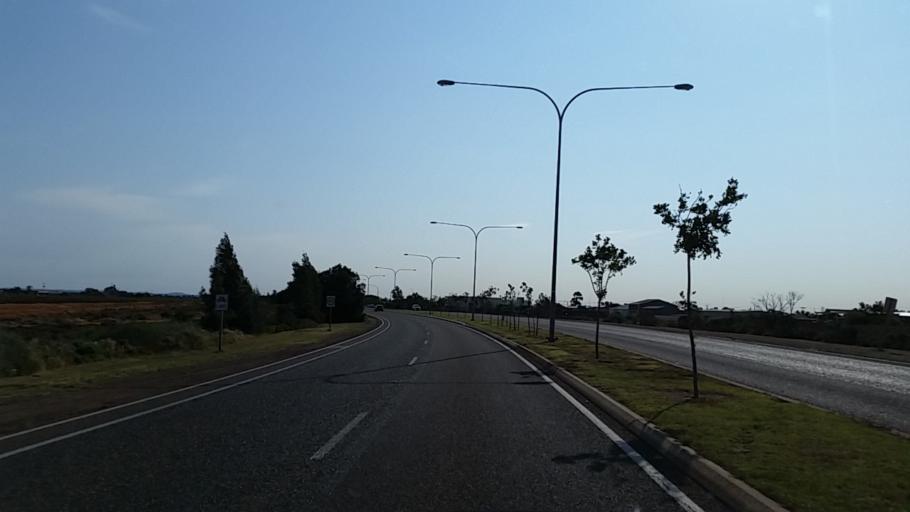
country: AU
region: South Australia
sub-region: Whyalla
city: Whyalla
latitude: -33.0399
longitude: 137.5565
